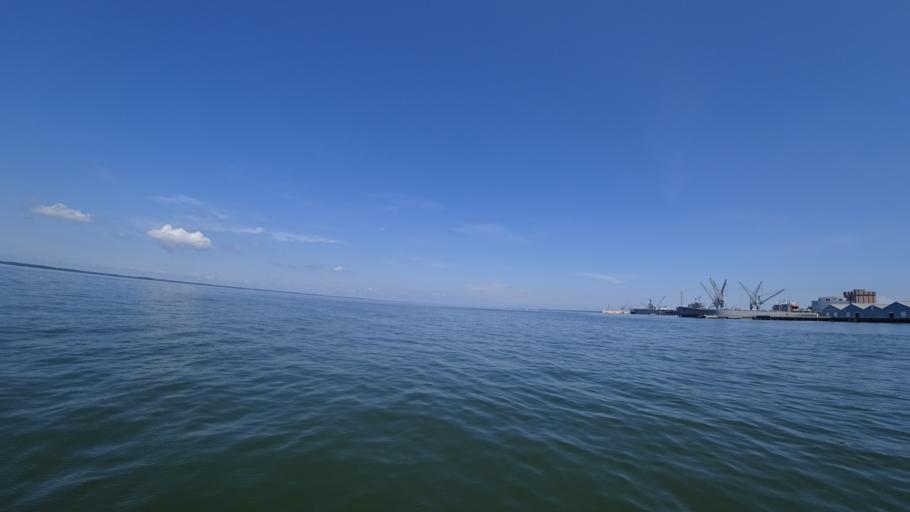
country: US
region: Virginia
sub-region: City of Newport News
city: Newport News
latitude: 36.9681
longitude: -76.4341
